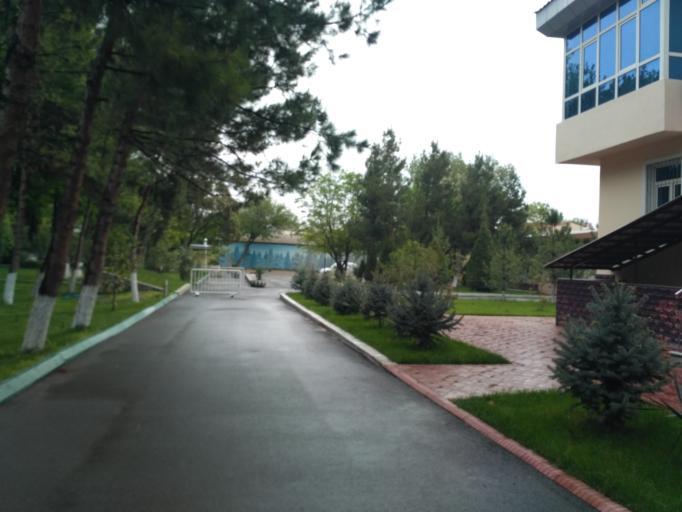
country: UZ
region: Toshkent
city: Salor
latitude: 41.3433
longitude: 69.3573
